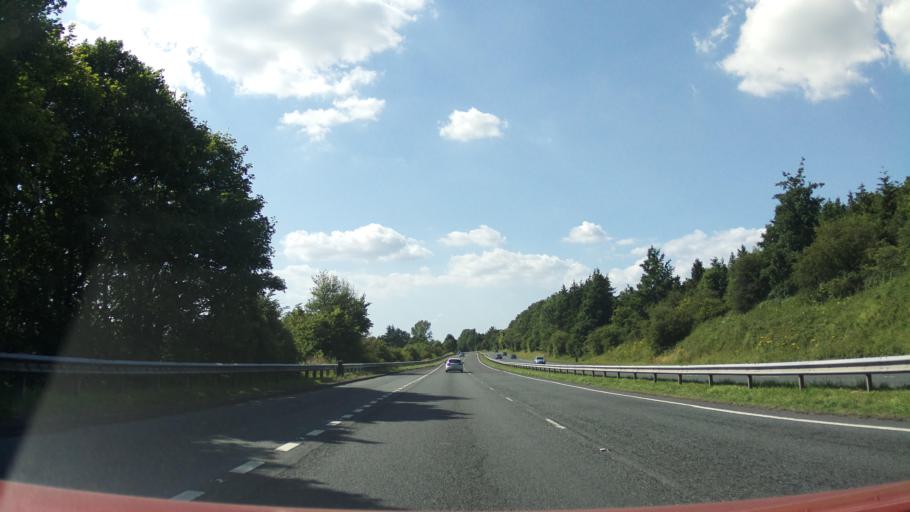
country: GB
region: England
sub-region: Worcestershire
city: Barnt Green
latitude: 52.3257
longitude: -2.0118
